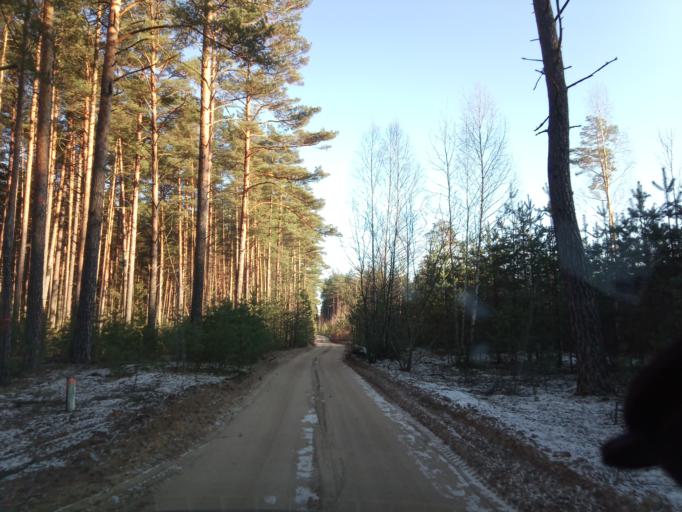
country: LT
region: Alytaus apskritis
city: Druskininkai
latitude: 53.9568
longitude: 23.8682
